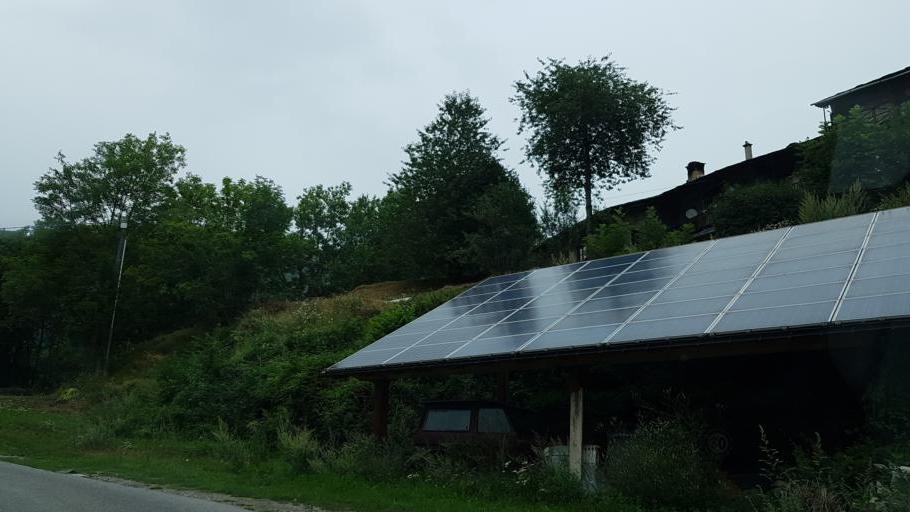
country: IT
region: Piedmont
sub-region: Provincia di Cuneo
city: Stroppo
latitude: 44.5101
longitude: 7.1291
